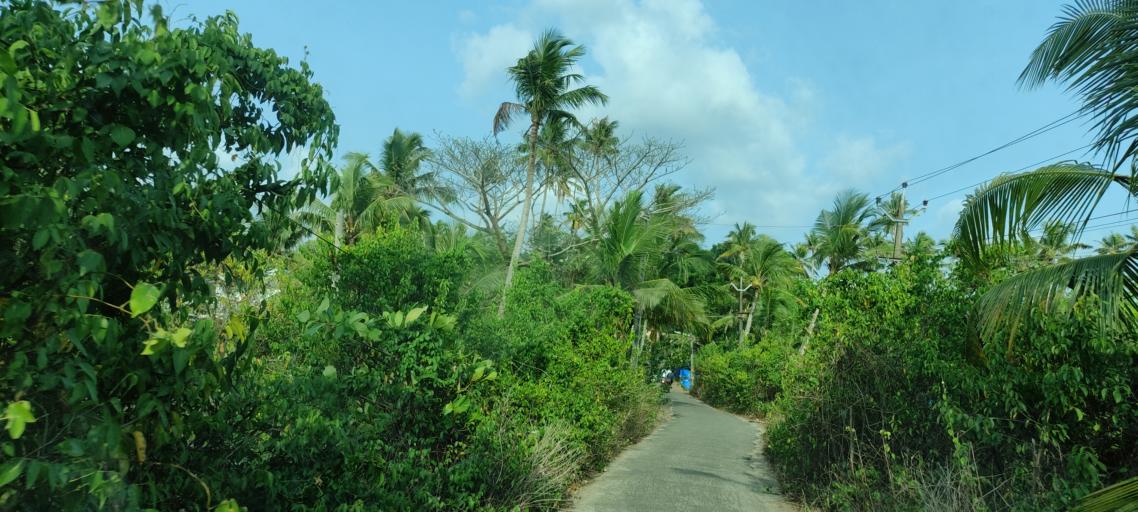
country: IN
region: Kerala
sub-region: Alappuzha
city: Vayalar
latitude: 9.7275
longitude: 76.2892
